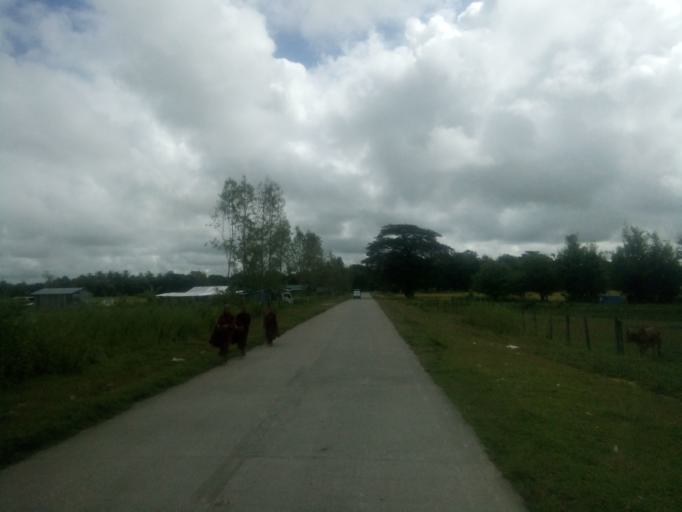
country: MM
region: Bago
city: Nyaunglebin
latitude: 17.9233
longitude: 96.5080
